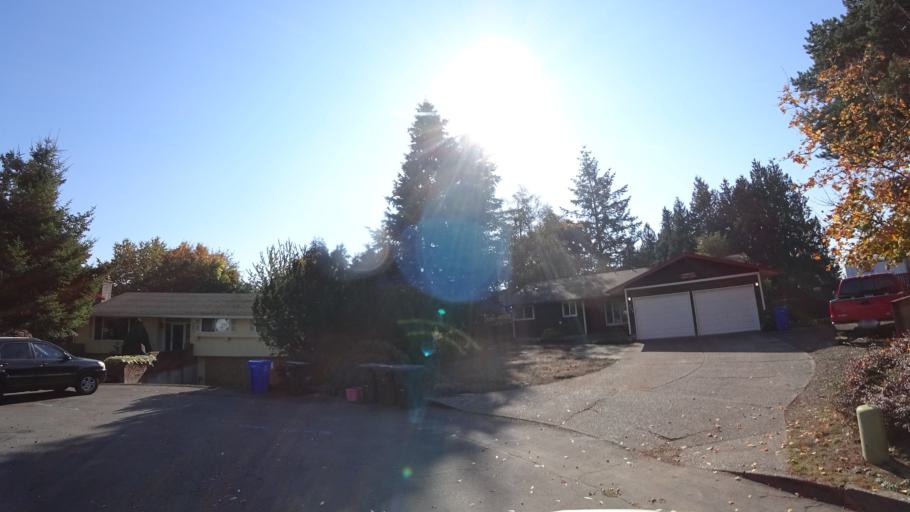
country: US
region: Oregon
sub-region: Multnomah County
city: Gresham
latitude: 45.4996
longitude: -122.4437
